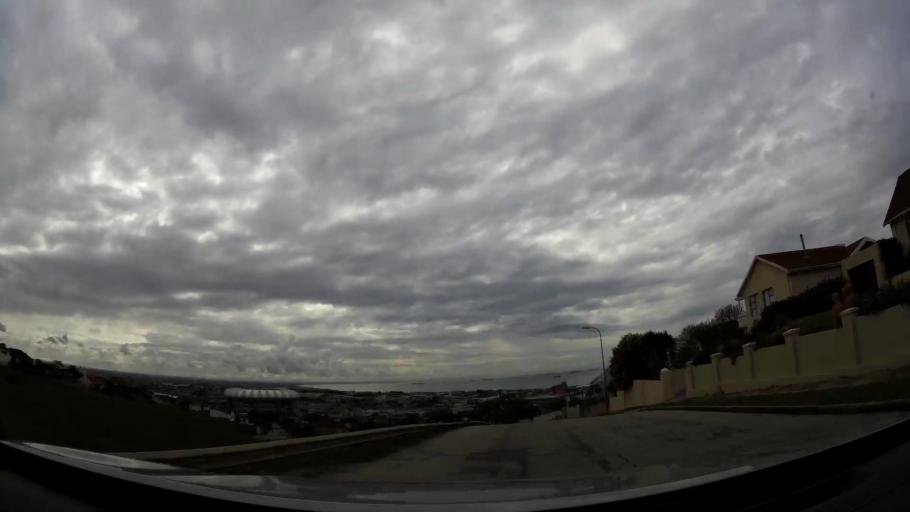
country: ZA
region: Eastern Cape
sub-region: Nelson Mandela Bay Metropolitan Municipality
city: Port Elizabeth
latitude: -33.9486
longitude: 25.5958
